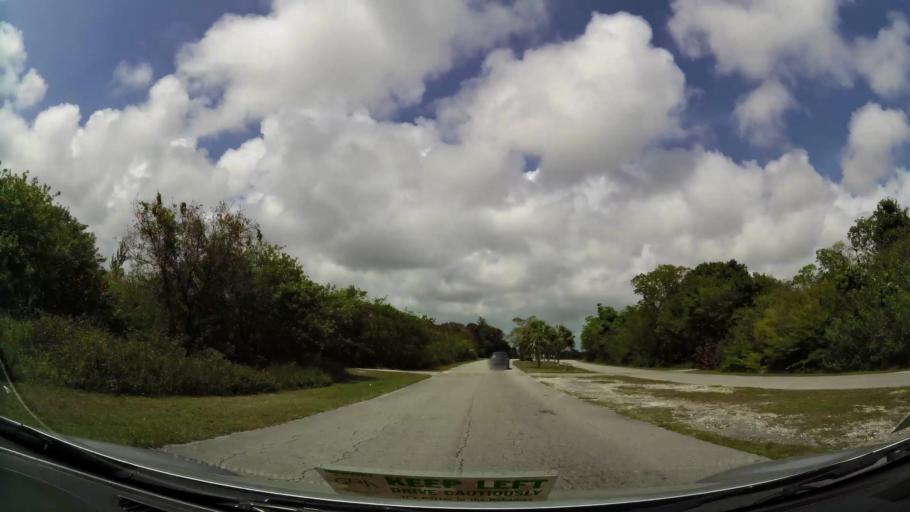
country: BS
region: Freeport
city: Freeport
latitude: 26.5103
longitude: -78.7093
